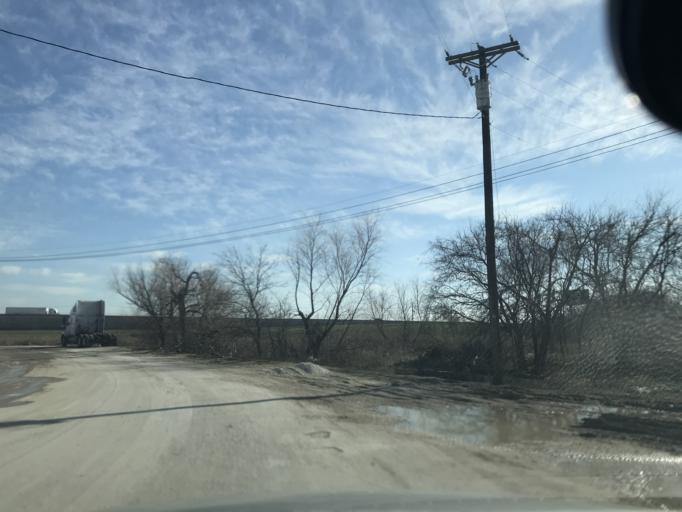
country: US
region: Texas
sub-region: Denton County
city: The Colony
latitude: 33.0838
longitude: -96.8556
